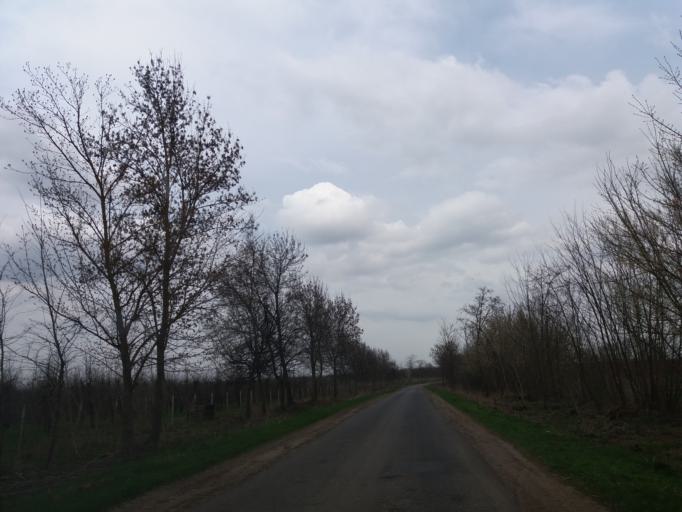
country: HU
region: Szabolcs-Szatmar-Bereg
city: Nyirtass
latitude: 48.1152
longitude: 22.0466
